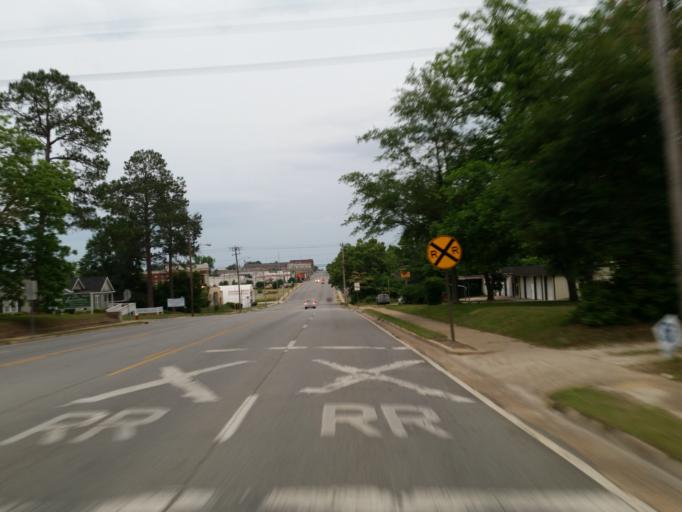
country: US
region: Georgia
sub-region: Crisp County
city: Cordele
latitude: 31.9770
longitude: -83.7829
